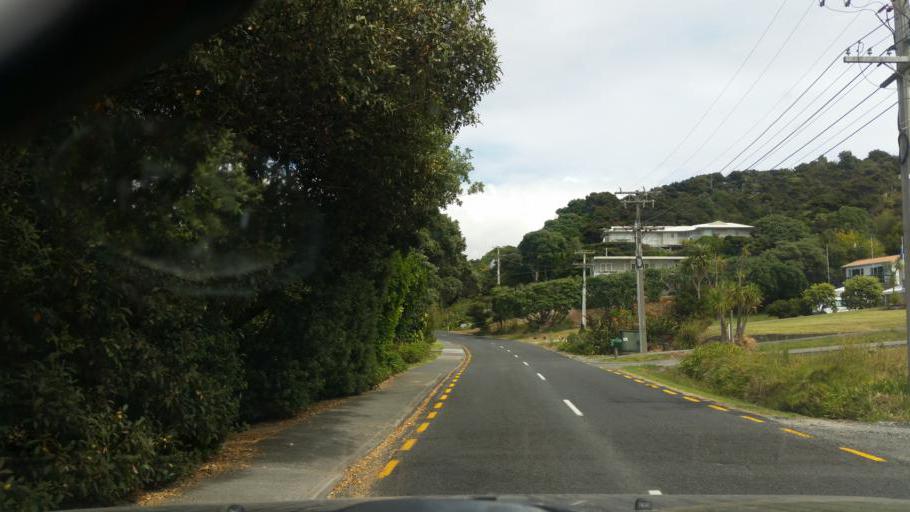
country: NZ
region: Auckland
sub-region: Auckland
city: Wellsford
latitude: -36.0812
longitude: 174.5943
